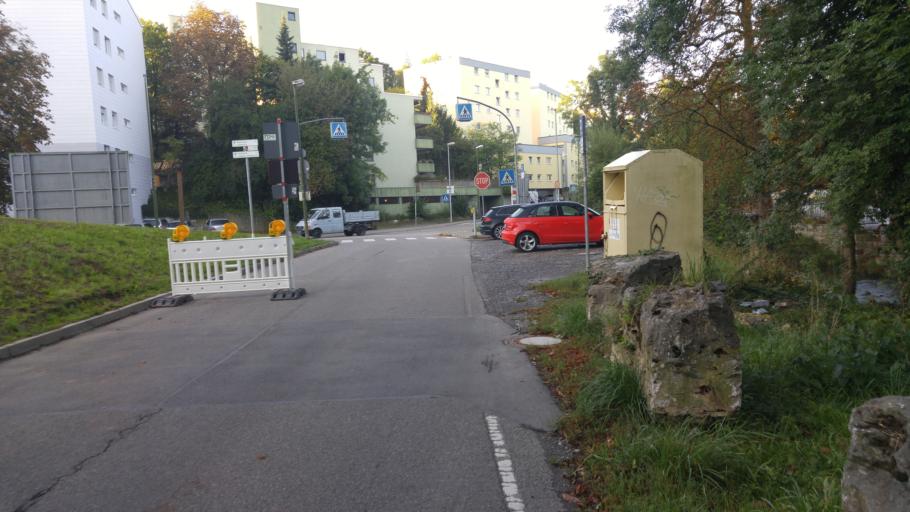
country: DE
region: Baden-Wuerttemberg
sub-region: Regierungsbezirk Stuttgart
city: Leonberg
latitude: 48.8018
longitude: 9.0101
